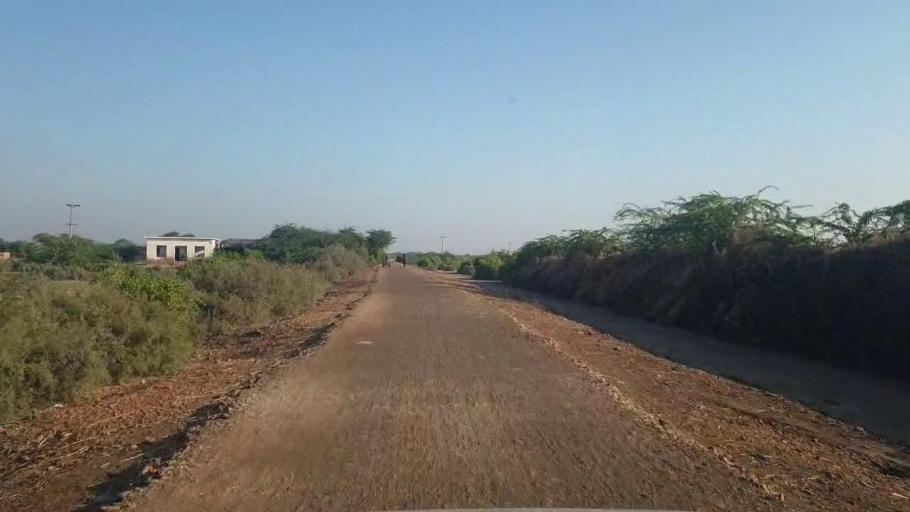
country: PK
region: Sindh
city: Badin
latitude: 24.7321
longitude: 68.8683
